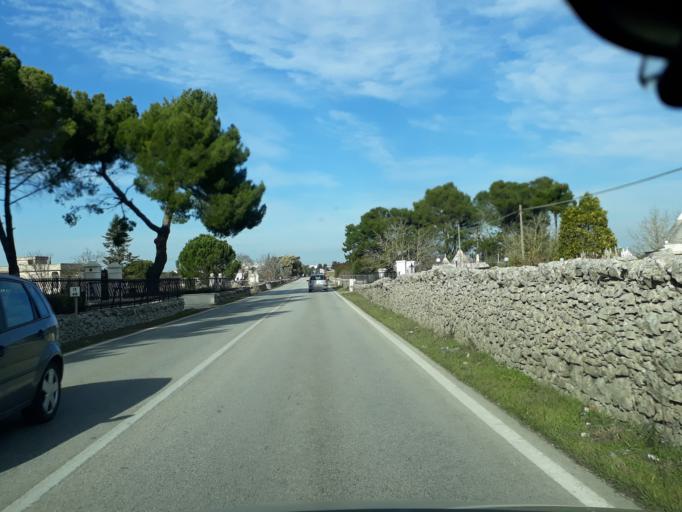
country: IT
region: Apulia
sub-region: Provincia di Taranto
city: Martina Franca
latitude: 40.7228
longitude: 17.3327
